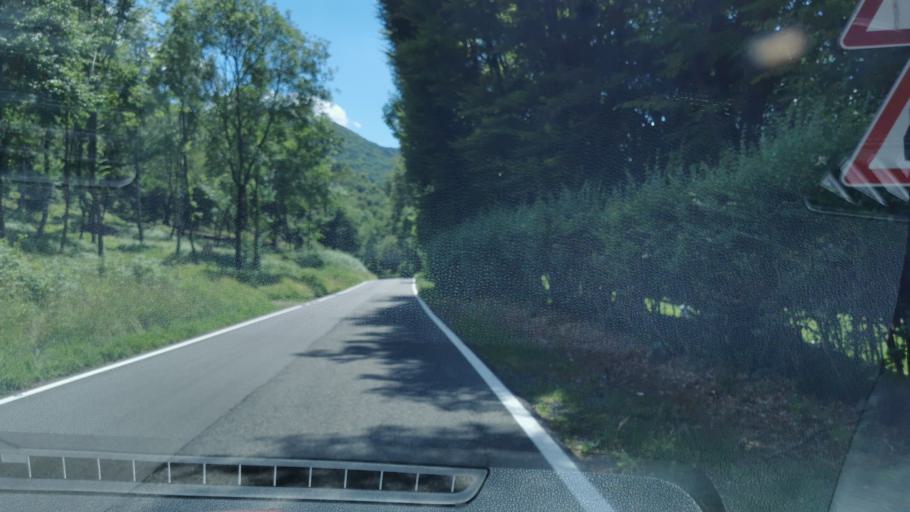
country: IT
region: Lombardy
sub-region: Provincia di Como
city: Lanzo d'Intelvi
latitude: 45.9744
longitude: 9.0366
